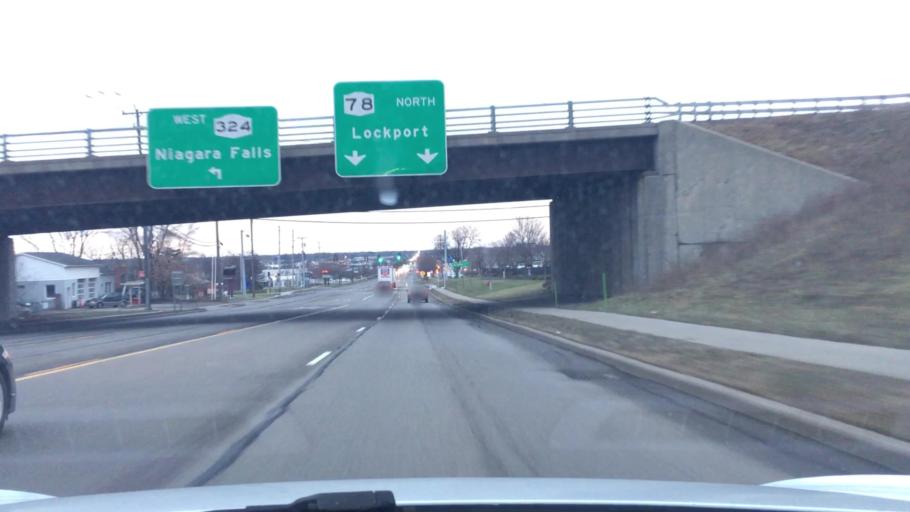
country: US
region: New York
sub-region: Erie County
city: Harris Hill
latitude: 42.9779
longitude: -78.6968
